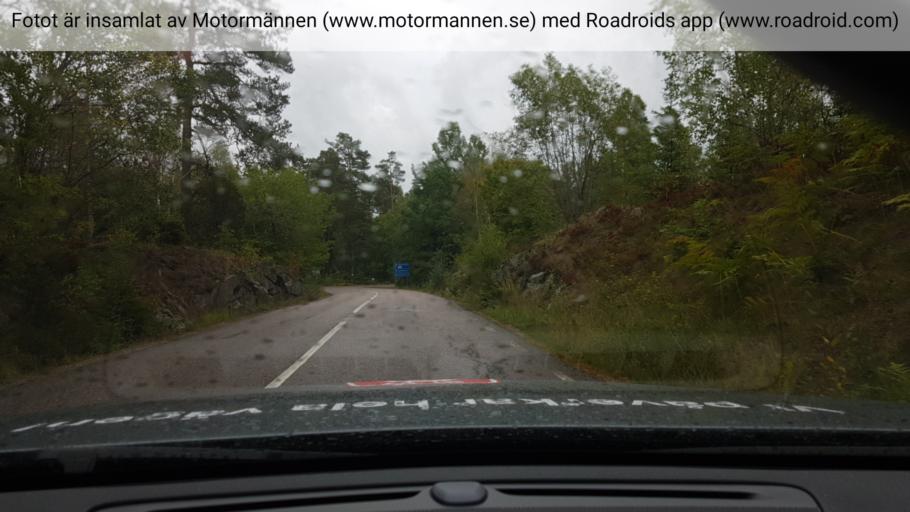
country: SE
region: Stockholm
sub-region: Nynashamns Kommun
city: Osmo
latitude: 59.0863
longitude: 17.9003
